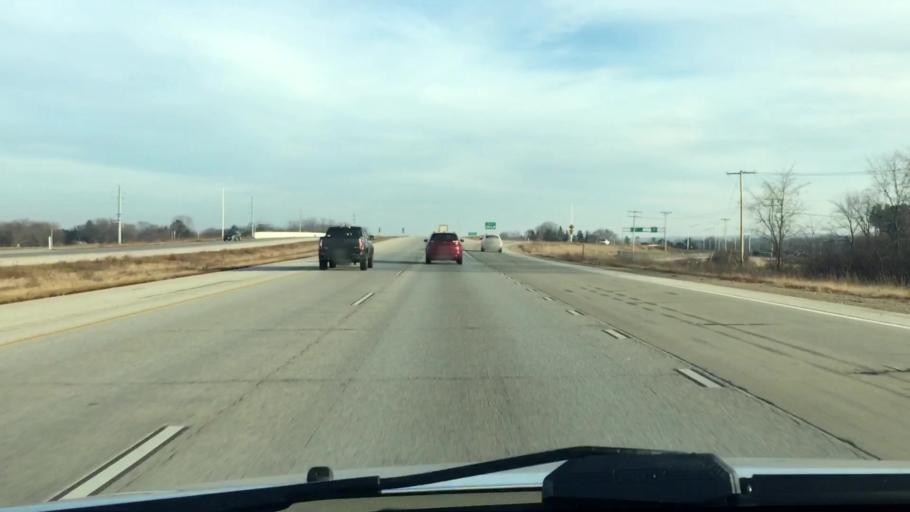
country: US
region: Wisconsin
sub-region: Waukesha County
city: Delafield
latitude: 43.0623
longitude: -88.4480
